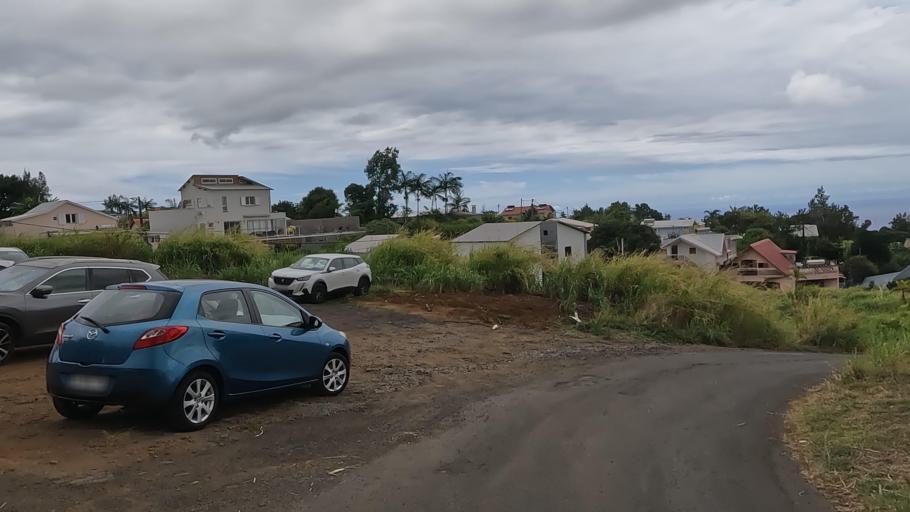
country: RE
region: Reunion
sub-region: Reunion
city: Le Tampon
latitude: -21.3113
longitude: 55.5366
